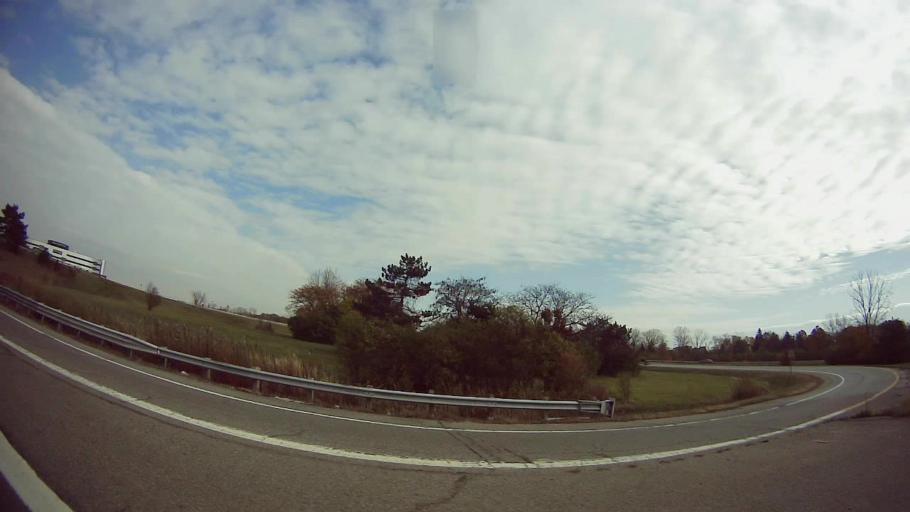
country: US
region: Michigan
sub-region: Oakland County
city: Troy
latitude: 42.5987
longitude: -83.1620
